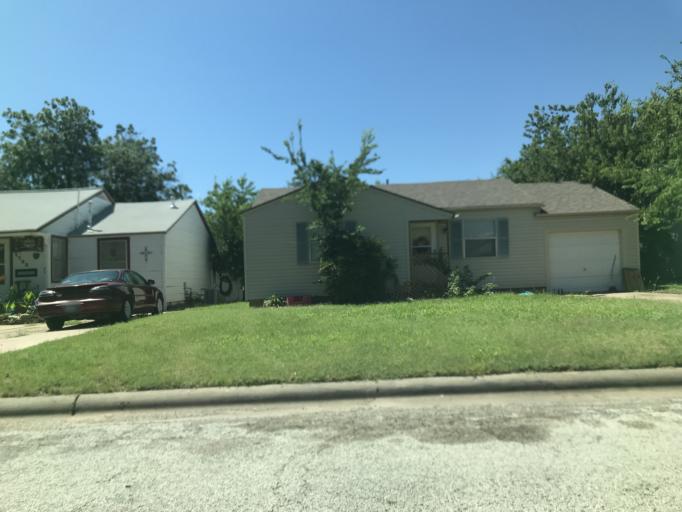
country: US
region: Texas
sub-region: Taylor County
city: Abilene
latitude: 32.4220
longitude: -99.7444
